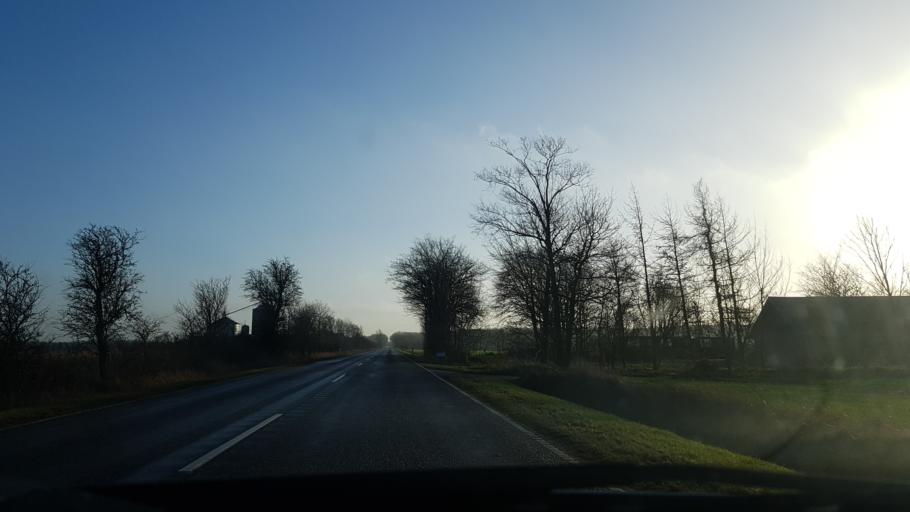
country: DK
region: South Denmark
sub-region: Tonder Kommune
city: Toftlund
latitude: 55.2320
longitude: 9.1678
